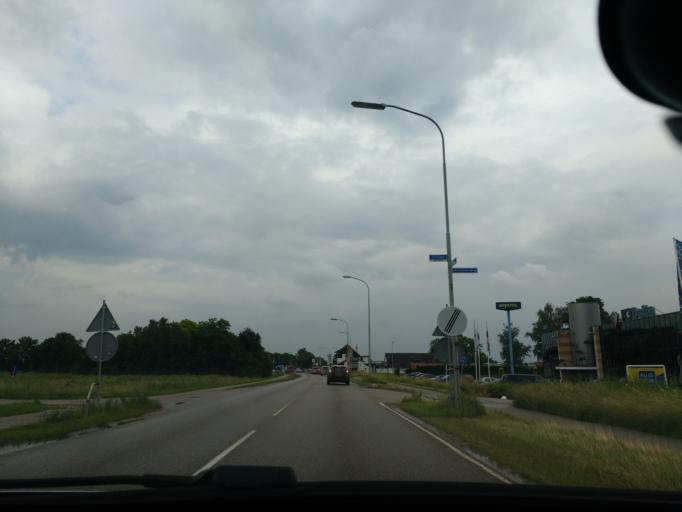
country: NL
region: Gelderland
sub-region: Gemeente Overbetuwe
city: Oosterhout
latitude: 51.8901
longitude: 5.8386
